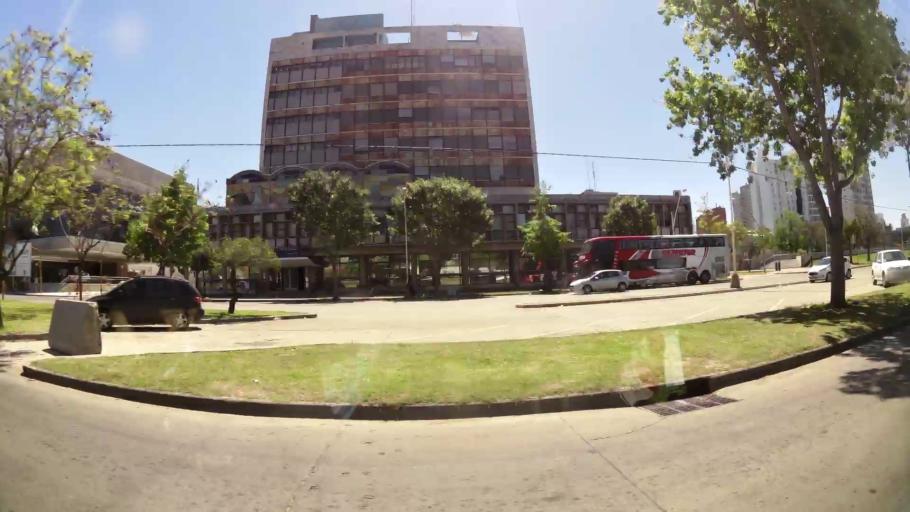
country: AR
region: Santa Fe
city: Santa Fe de la Vera Cruz
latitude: -31.6495
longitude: -60.7046
